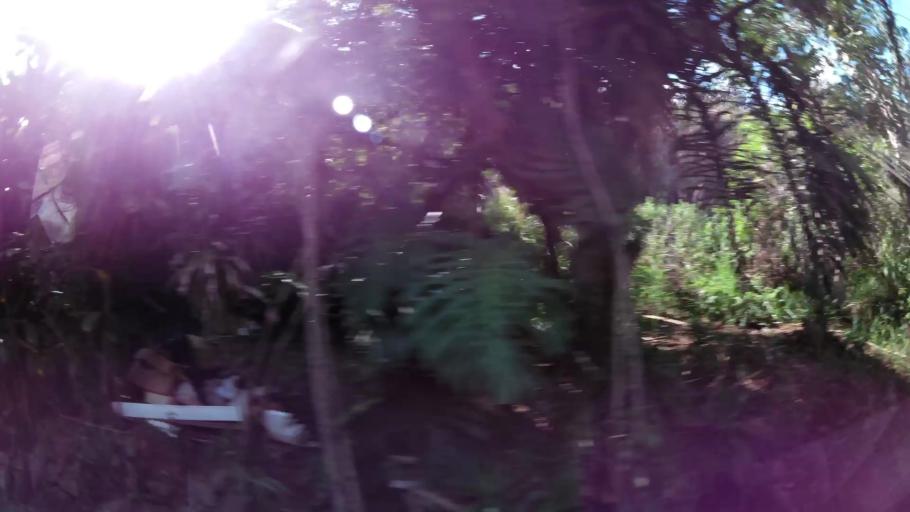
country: CO
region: Valle del Cauca
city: Cali
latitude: 3.4380
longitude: -76.5547
